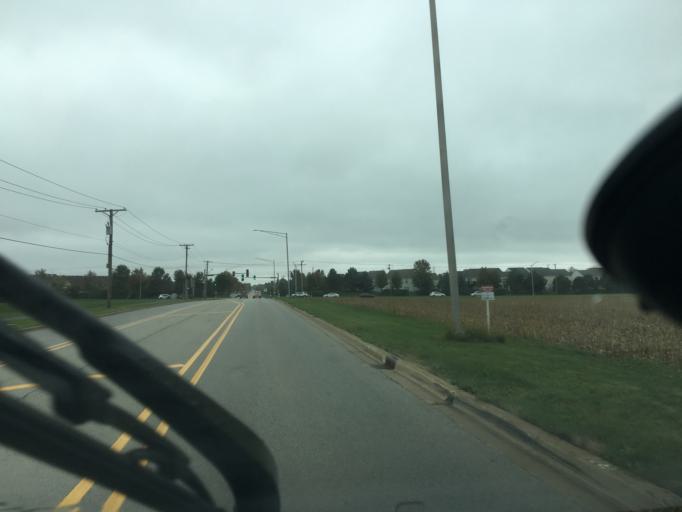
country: US
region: Illinois
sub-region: Will County
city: Plainfield
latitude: 41.6659
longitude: -88.2213
